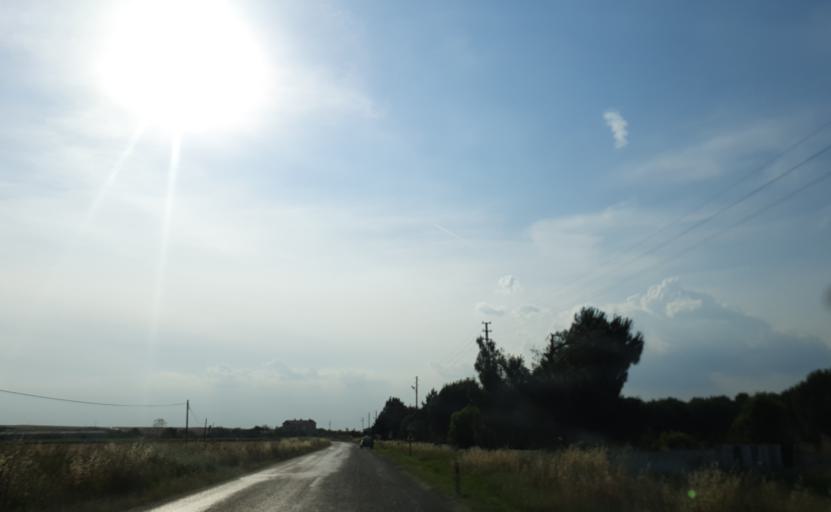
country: TR
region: Tekirdag
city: Muratli
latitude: 41.2161
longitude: 27.4342
